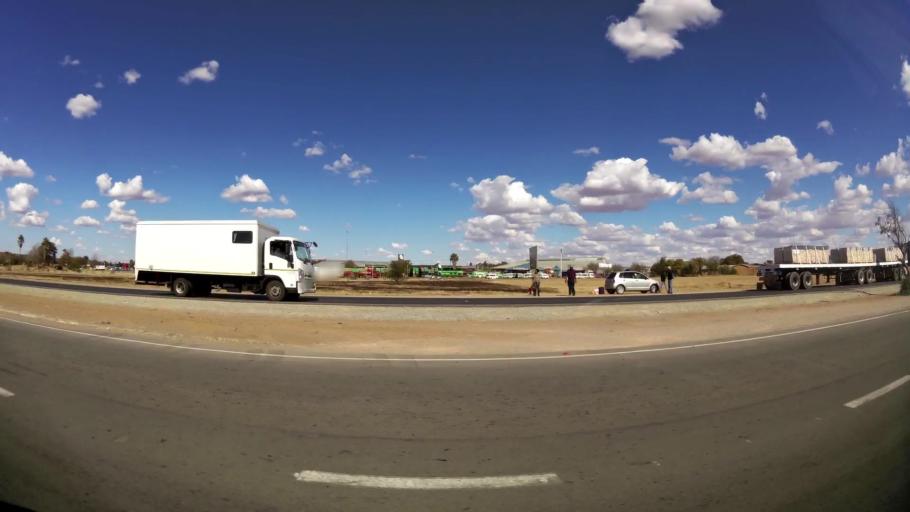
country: ZA
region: North-West
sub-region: Dr Kenneth Kaunda District Municipality
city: Klerksdorp
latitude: -26.8688
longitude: 26.6250
